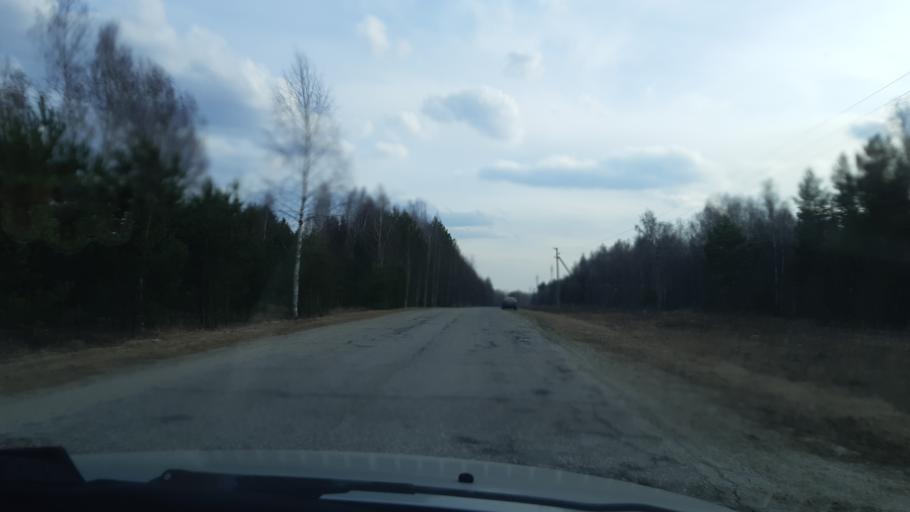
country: RU
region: Vladimir
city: Nikologory
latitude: 56.1147
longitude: 41.9846
